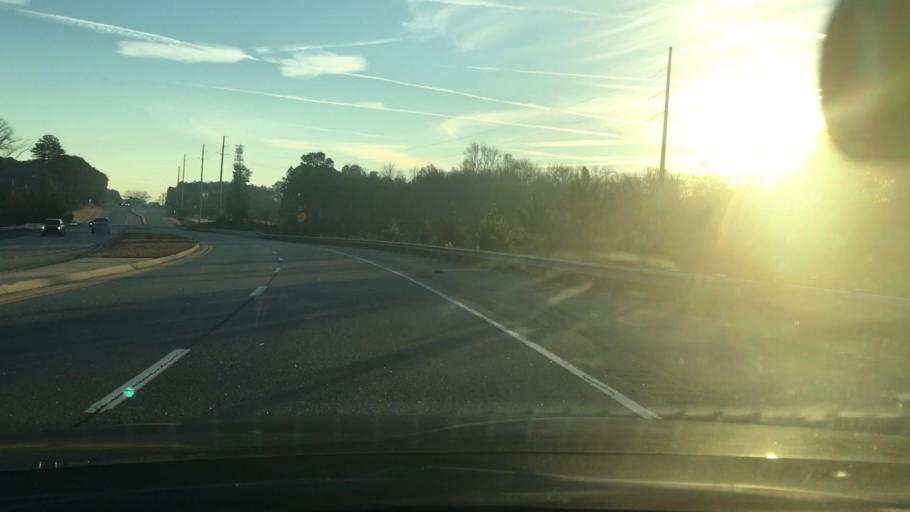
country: US
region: Georgia
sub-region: Coweta County
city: Senoia
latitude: 33.3414
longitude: -84.5405
